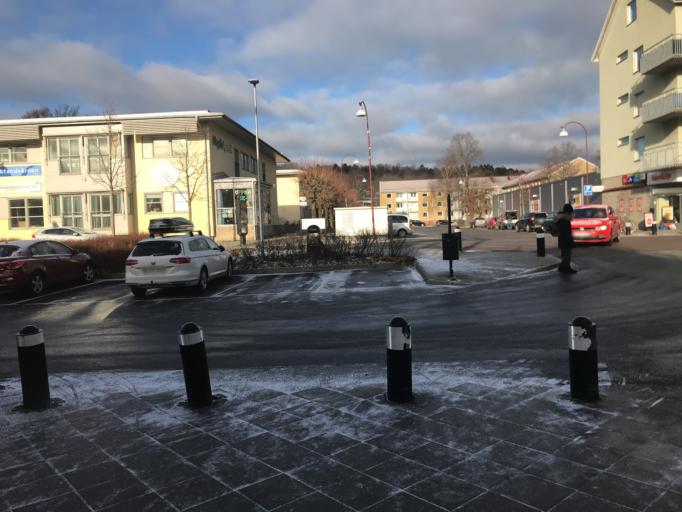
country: SE
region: Vaestra Goetaland
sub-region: Harryda Kommun
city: Molnlycke
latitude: 57.6579
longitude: 12.1140
